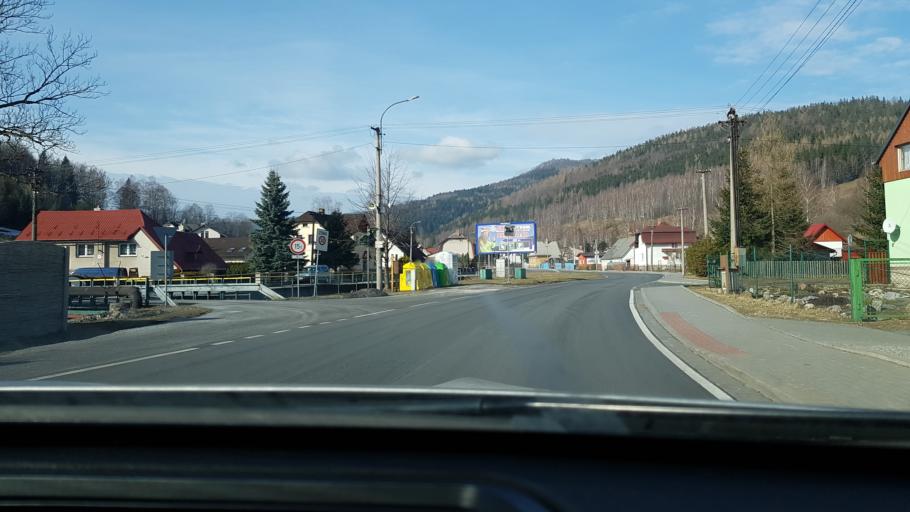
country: CZ
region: Olomoucky
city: Vapenna
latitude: 50.2261
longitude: 17.1288
